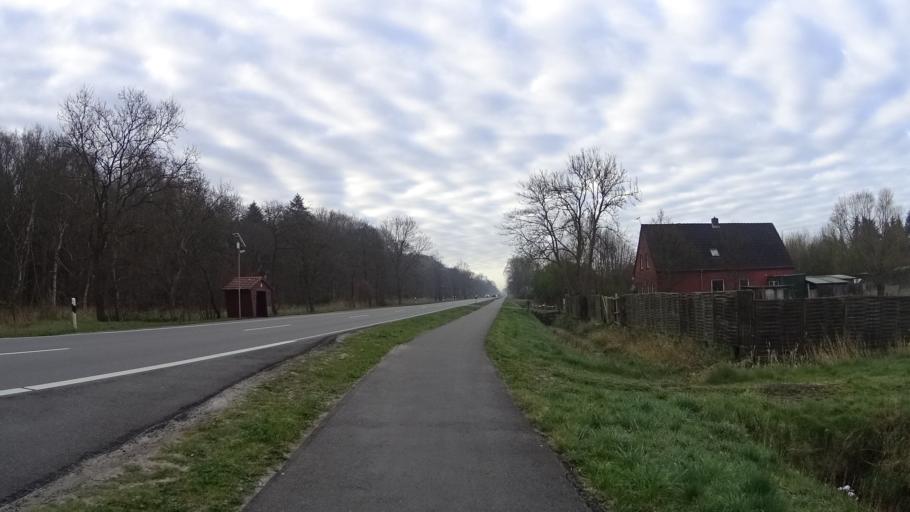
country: DE
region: Lower Saxony
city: Lutetsburg
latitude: 53.5751
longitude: 7.2361
